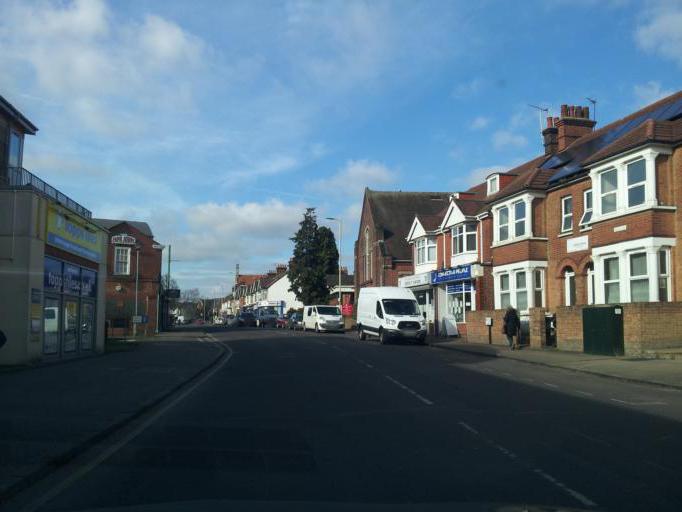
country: GB
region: England
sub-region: Hertfordshire
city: St Albans
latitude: 51.7526
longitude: -0.3164
